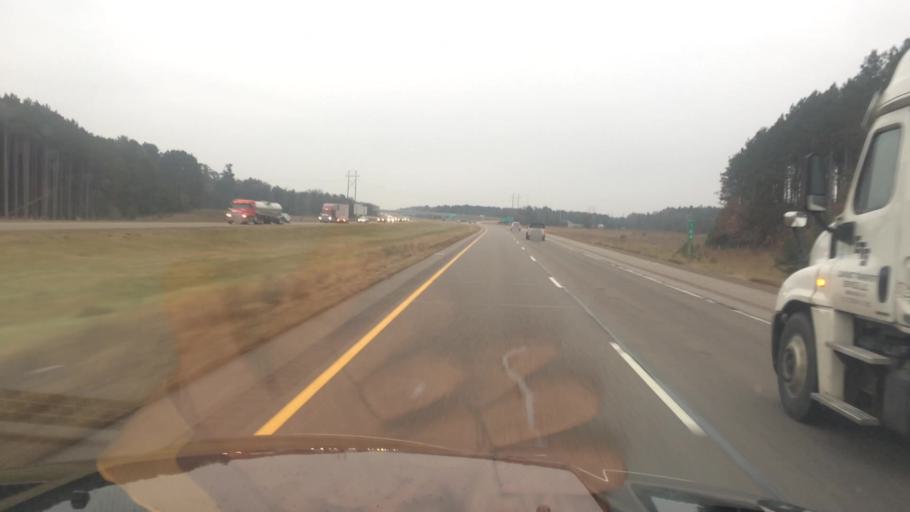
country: US
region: Wisconsin
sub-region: Portage County
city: Stevens Point
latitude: 44.5774
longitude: -89.6037
